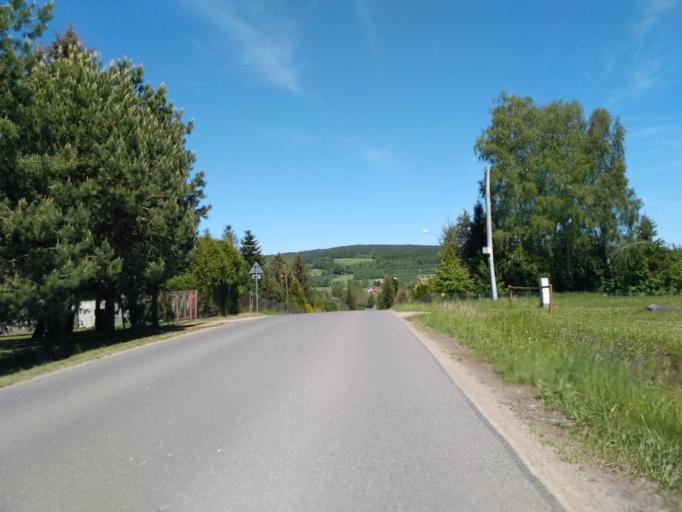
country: PL
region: Subcarpathian Voivodeship
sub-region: Powiat sanocki
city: Nowosielce-Gniewosz
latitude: 49.5533
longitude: 22.0929
